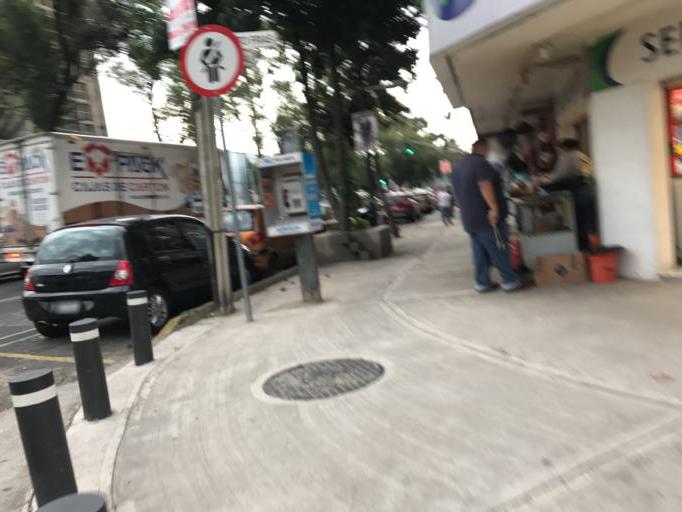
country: MX
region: Mexico City
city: Benito Juarez
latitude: 19.4014
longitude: -99.1591
